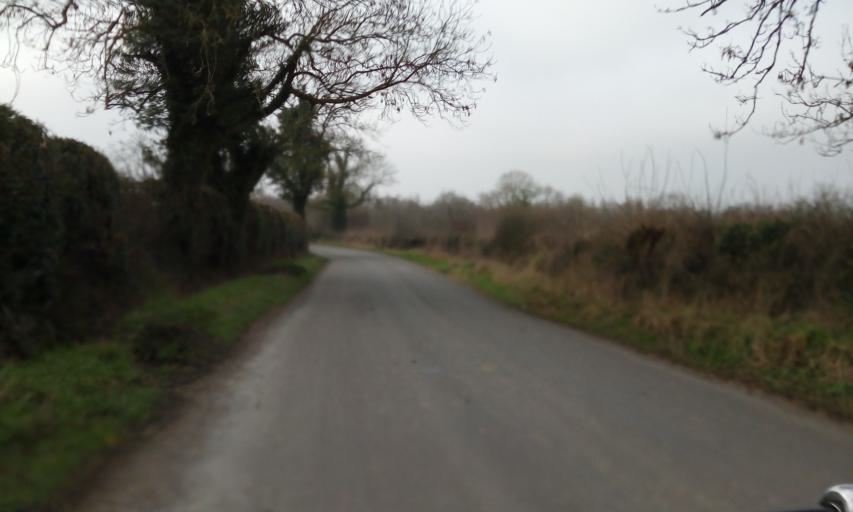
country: IE
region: Leinster
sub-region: Kilkenny
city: Kilkenny
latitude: 52.6637
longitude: -7.1876
